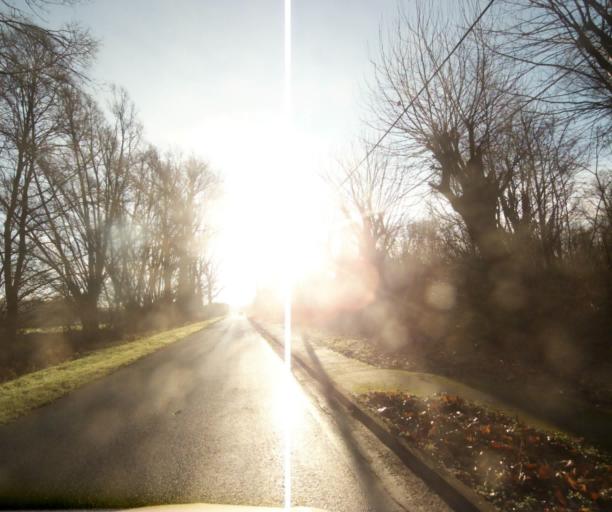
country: FR
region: Nord-Pas-de-Calais
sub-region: Departement du Nord
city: Onnaing
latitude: 50.3973
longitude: 3.5886
